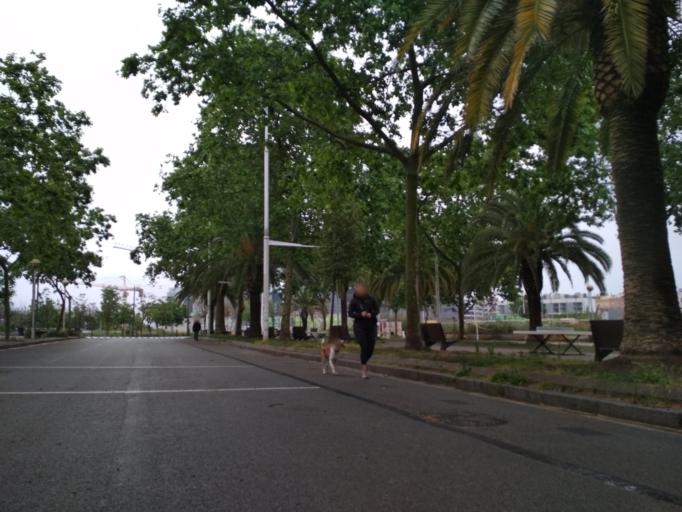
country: ES
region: Catalonia
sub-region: Provincia de Barcelona
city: Sant Marti
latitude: 41.4029
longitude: 2.1841
